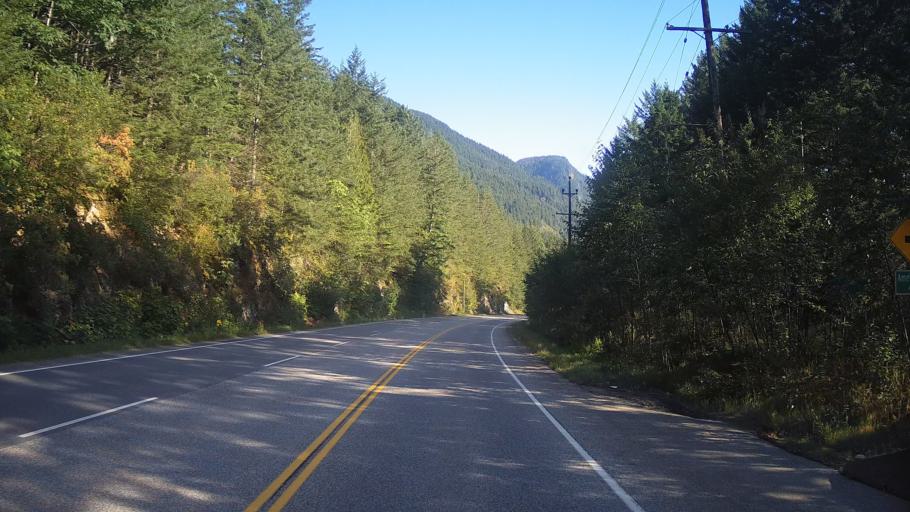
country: CA
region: British Columbia
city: Hope
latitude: 49.4226
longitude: -121.4380
